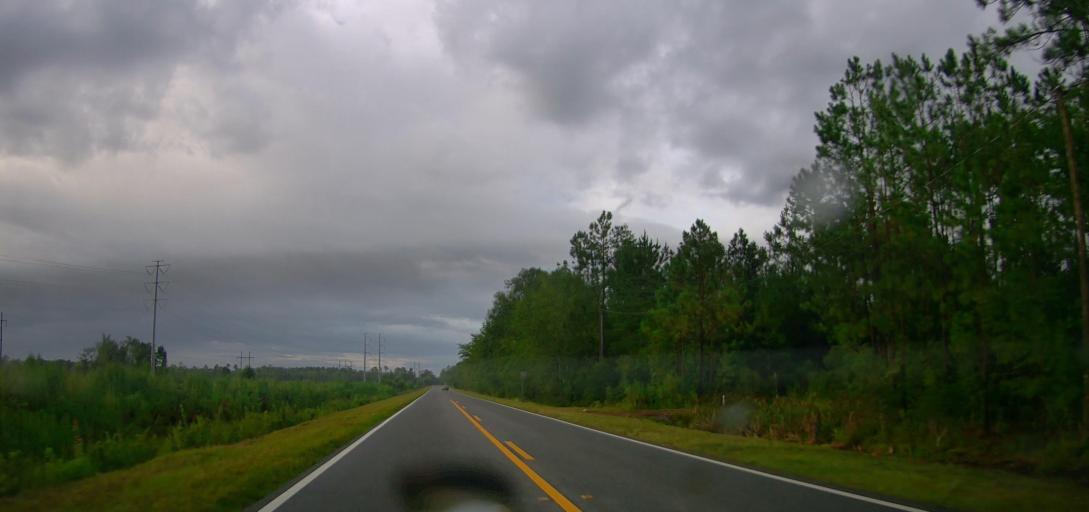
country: US
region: Georgia
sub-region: Ware County
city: Deenwood
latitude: 31.1972
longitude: -82.4015
